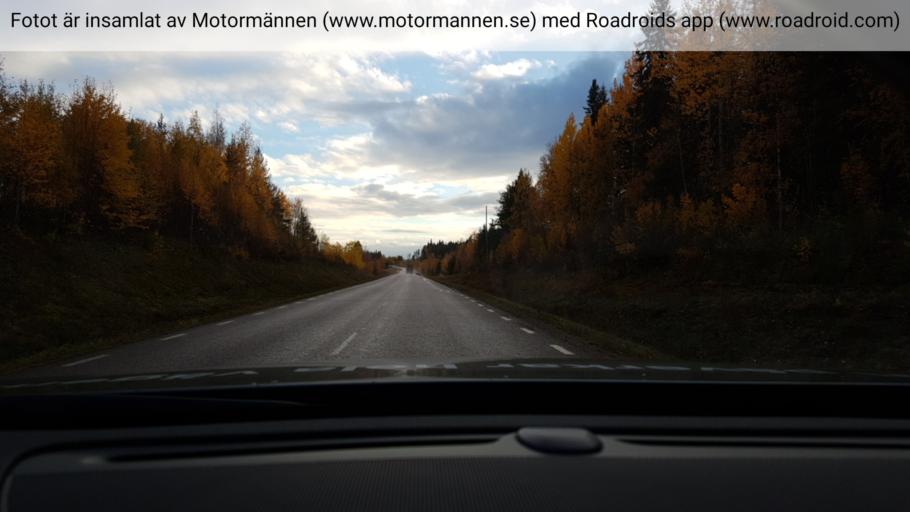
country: SE
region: Norrbotten
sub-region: Overkalix Kommun
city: OEverkalix
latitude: 66.7776
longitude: 22.6972
